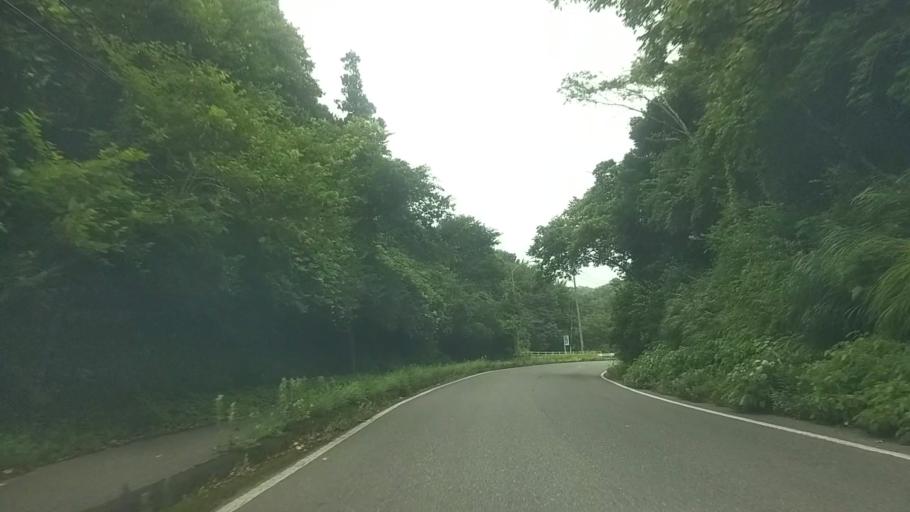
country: JP
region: Chiba
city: Kawaguchi
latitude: 35.2420
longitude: 140.0354
